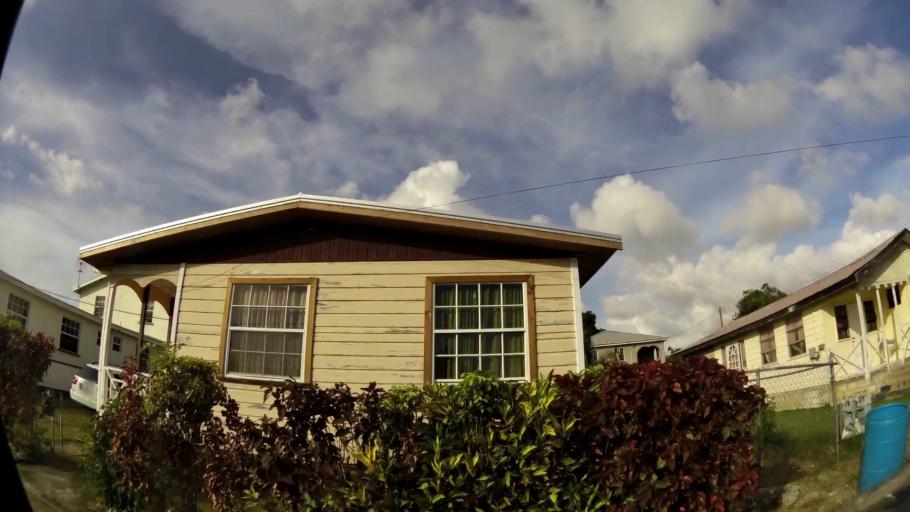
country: BB
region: Christ Church
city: Oistins
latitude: 13.0838
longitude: -59.5703
